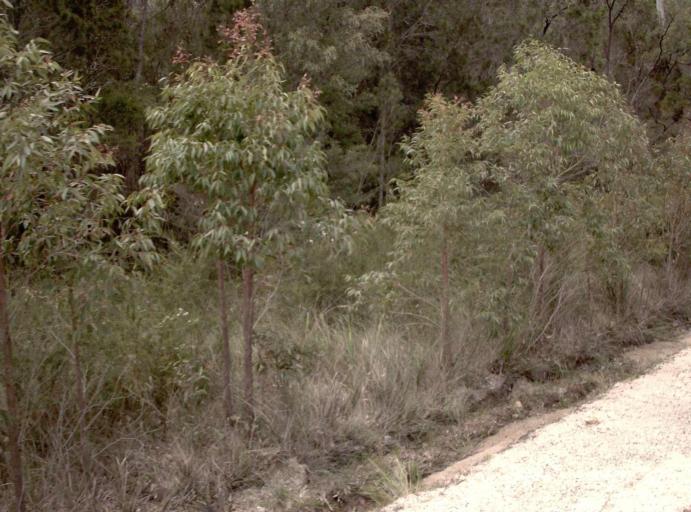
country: AU
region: New South Wales
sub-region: Bega Valley
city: Eden
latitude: -37.4558
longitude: 149.6150
